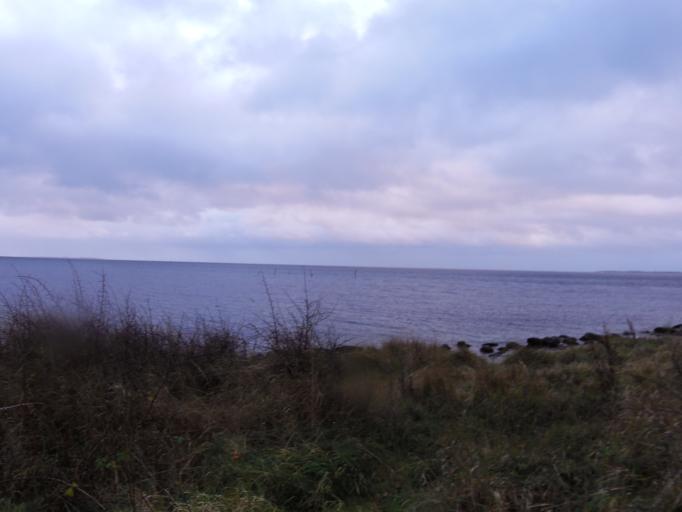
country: DK
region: Central Jutland
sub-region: Arhus Kommune
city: Beder
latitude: 56.0196
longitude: 10.2796
